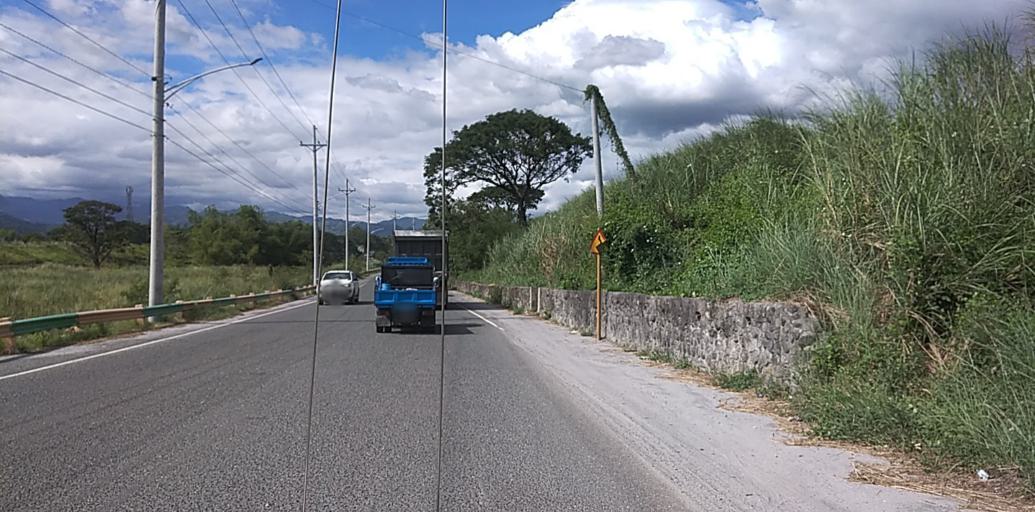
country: PH
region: Central Luzon
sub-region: Province of Pampanga
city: Dolores
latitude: 15.0884
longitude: 120.5388
